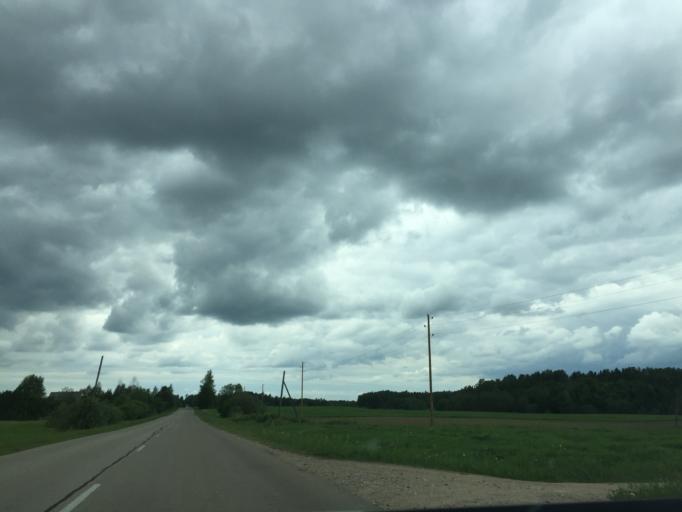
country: LV
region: Dagda
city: Dagda
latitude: 56.1094
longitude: 27.4881
